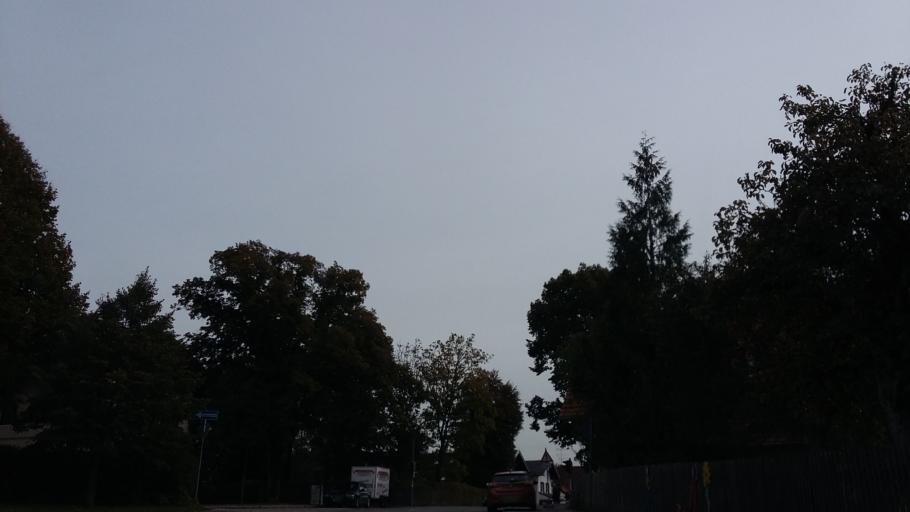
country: DE
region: Bavaria
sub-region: Upper Bavaria
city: Berg
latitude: 47.9576
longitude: 11.3629
